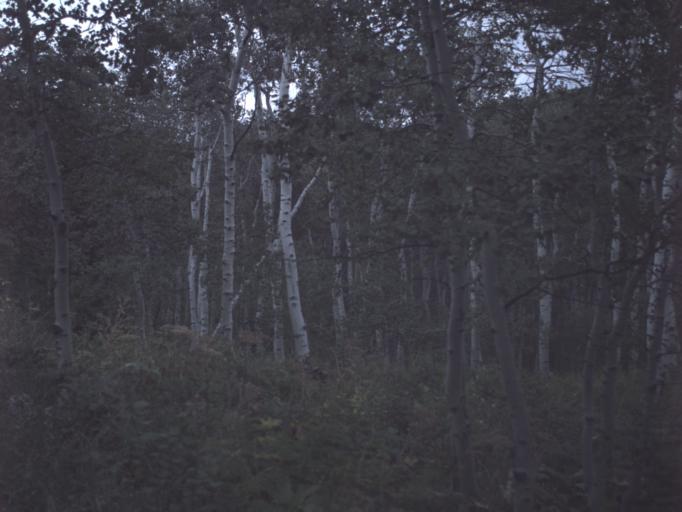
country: US
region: Utah
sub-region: Utah County
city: Lindon
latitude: 40.4173
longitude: -111.6068
